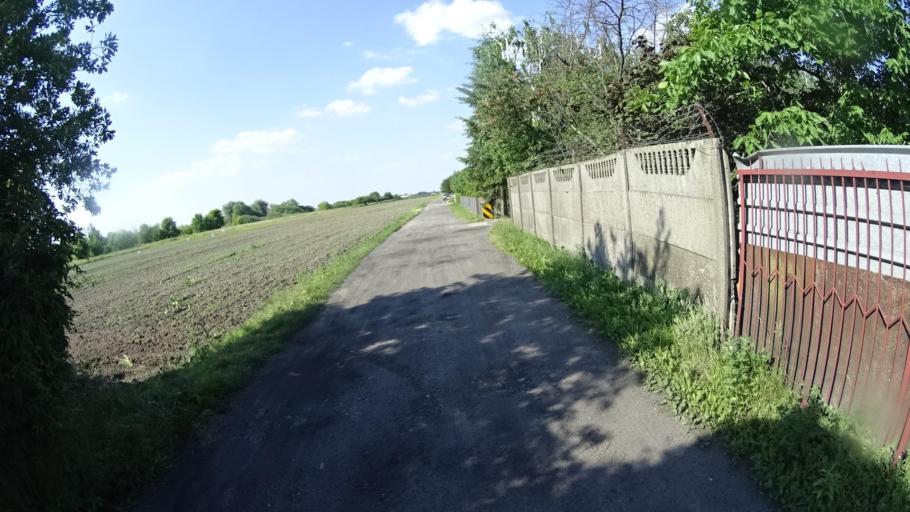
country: PL
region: Masovian Voivodeship
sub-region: Powiat warszawski zachodni
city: Ozarow Mazowiecki
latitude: 52.1918
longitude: 20.7556
